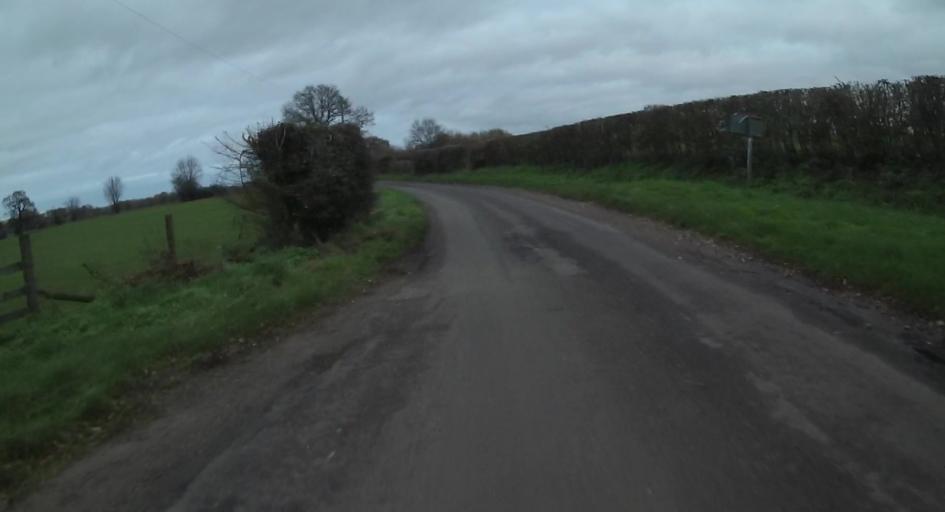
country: GB
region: England
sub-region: Hampshire
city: Long Sutton
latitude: 51.2176
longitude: -0.9057
